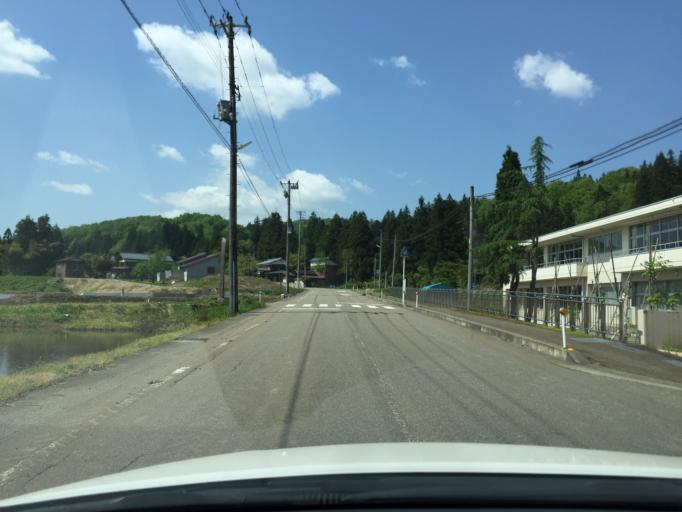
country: JP
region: Niigata
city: Tochio-honcho
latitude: 37.5011
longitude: 139.0580
